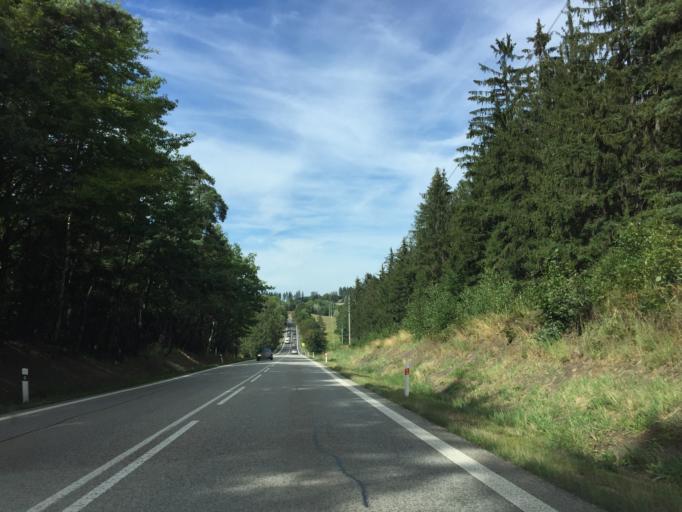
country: CZ
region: Central Bohemia
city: Votice
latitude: 49.5924
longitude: 14.6616
